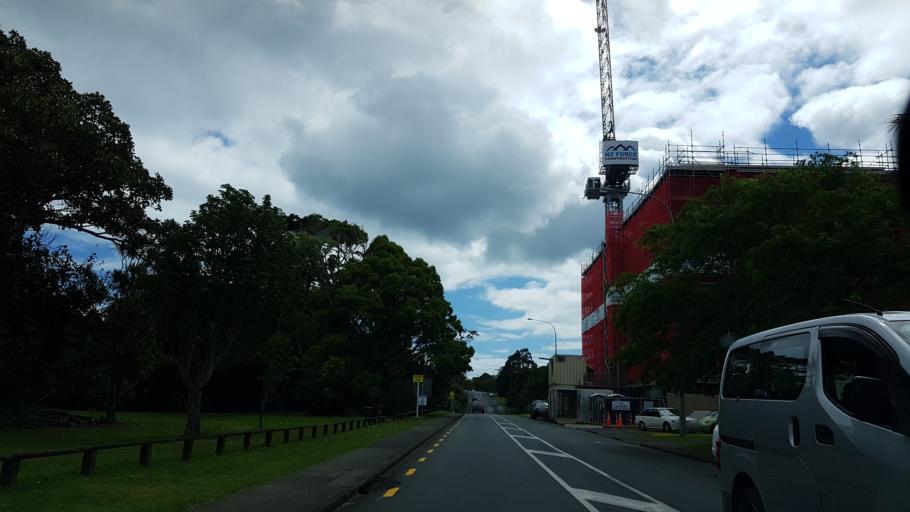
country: NZ
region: Auckland
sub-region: Auckland
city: North Shore
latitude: -36.7875
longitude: 174.7656
